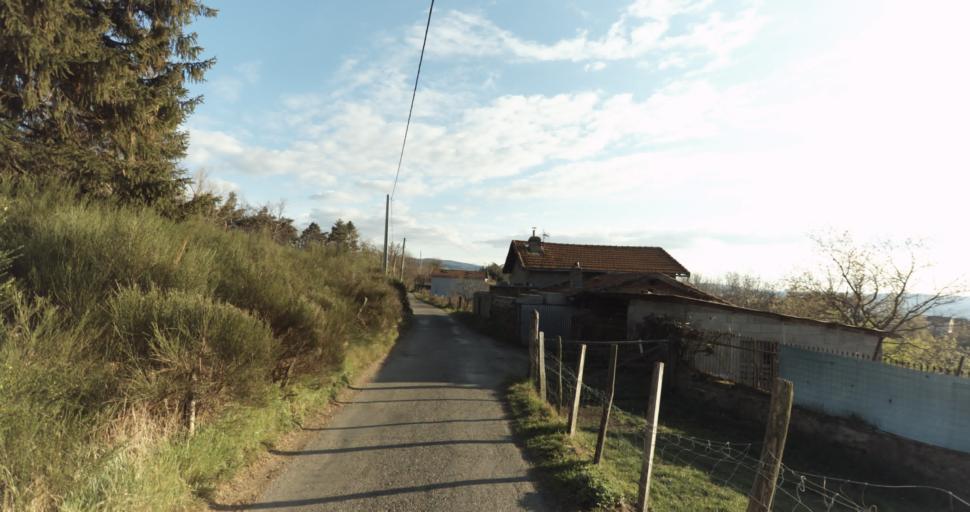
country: FR
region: Rhone-Alpes
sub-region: Departement de la Loire
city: Saint-Jean-Bonnefonds
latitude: 45.4637
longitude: 4.4464
